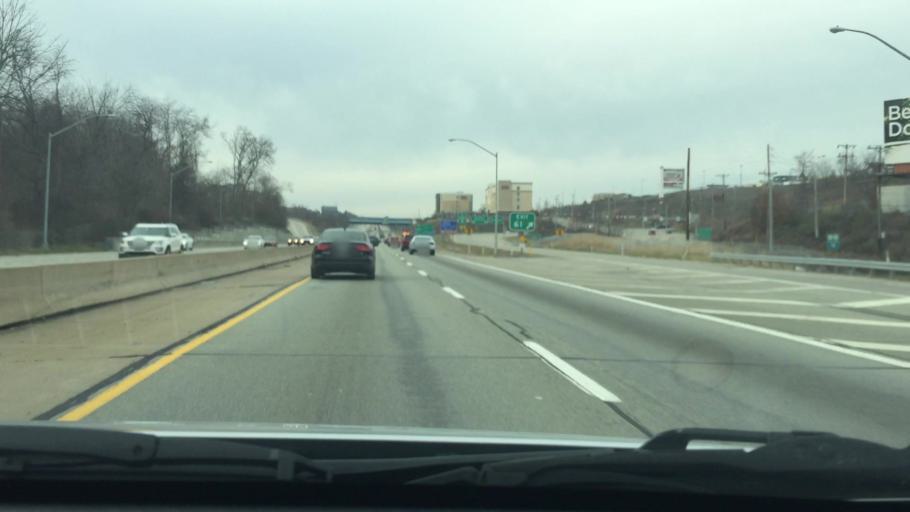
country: US
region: Pennsylvania
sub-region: Allegheny County
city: Rennerdale
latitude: 40.4353
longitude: -80.1457
